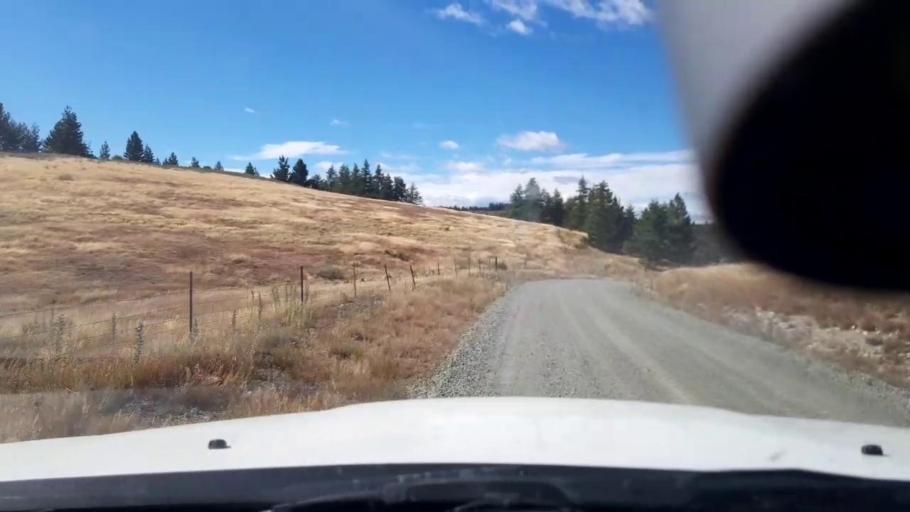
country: NZ
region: Canterbury
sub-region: Timaru District
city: Pleasant Point
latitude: -44.0114
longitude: 170.4727
